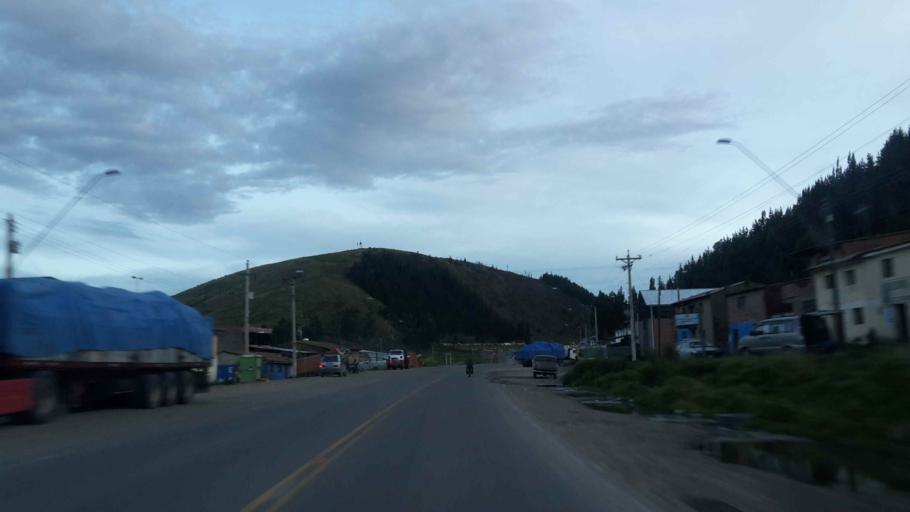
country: BO
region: Cochabamba
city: Colomi
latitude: -17.3721
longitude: -65.8348
